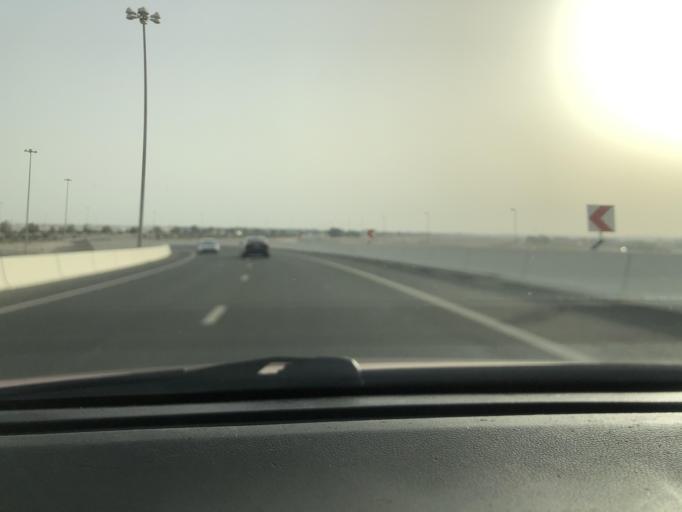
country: AE
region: Abu Dhabi
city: Abu Dhabi
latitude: 24.4176
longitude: 54.7118
